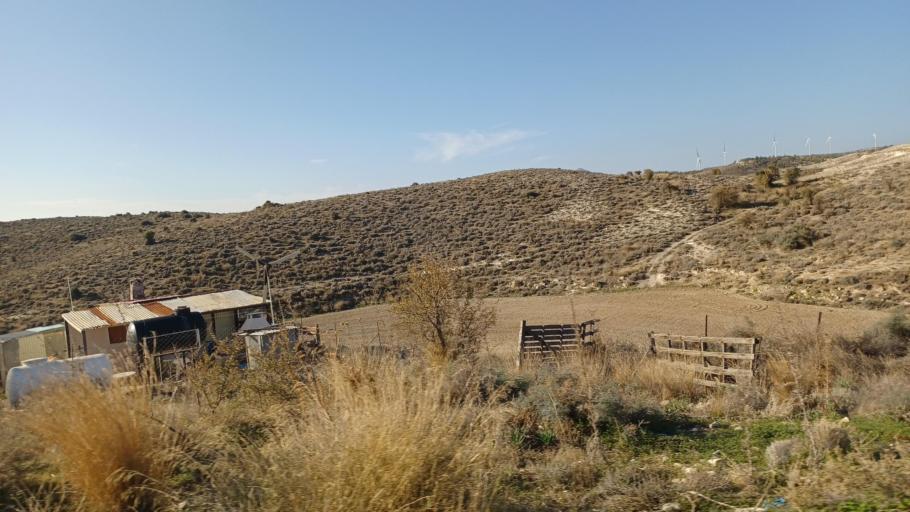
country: CY
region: Larnaka
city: Psevdas
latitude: 34.9406
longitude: 33.5216
